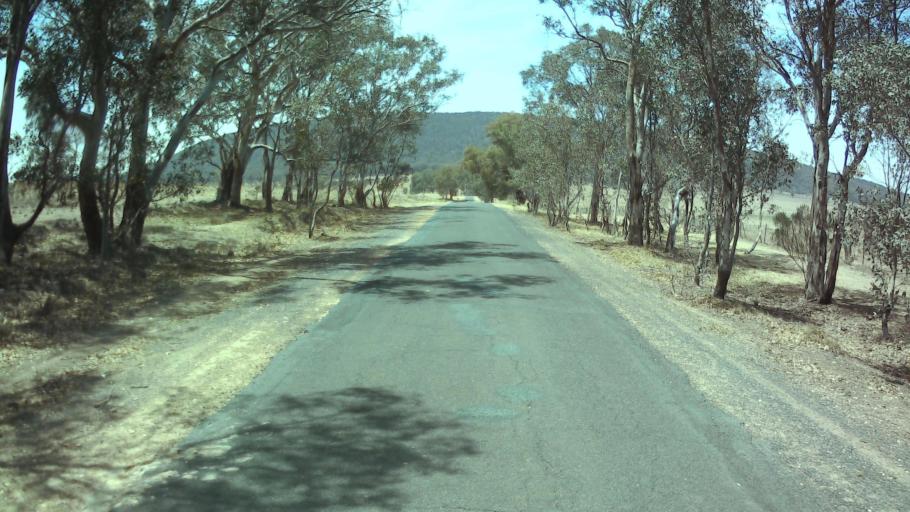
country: AU
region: New South Wales
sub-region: Weddin
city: Grenfell
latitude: -34.0306
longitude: 148.4328
